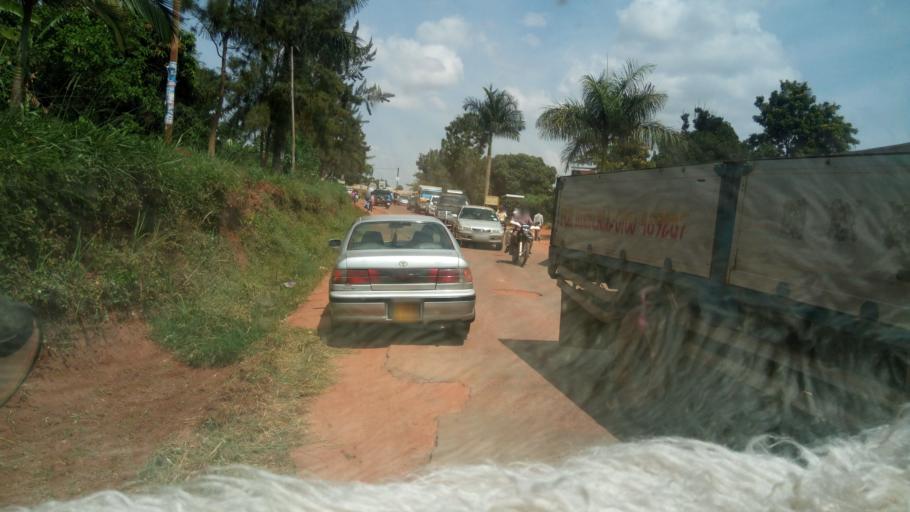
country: UG
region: Central Region
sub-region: Mukono District
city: Mukono
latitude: 0.3609
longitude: 32.7433
